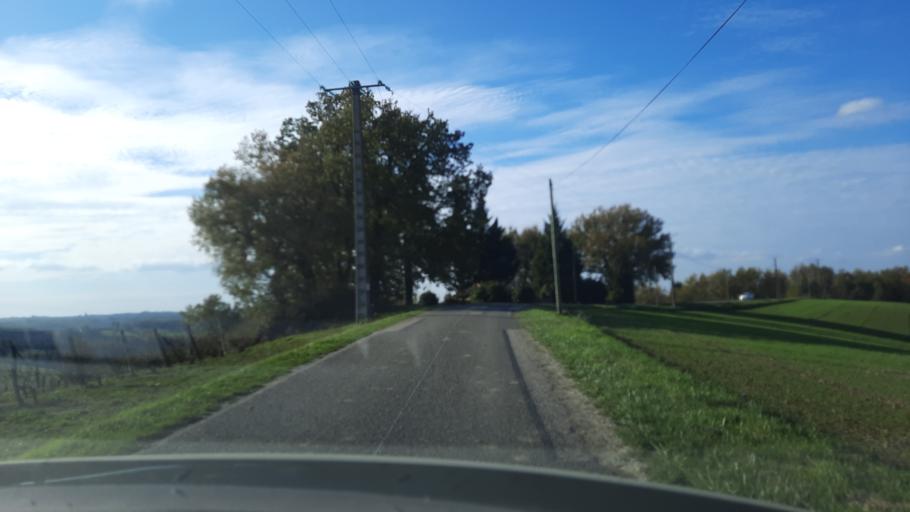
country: FR
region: Midi-Pyrenees
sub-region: Departement du Tarn-et-Garonne
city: Lafrancaise
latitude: 44.1470
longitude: 1.3015
